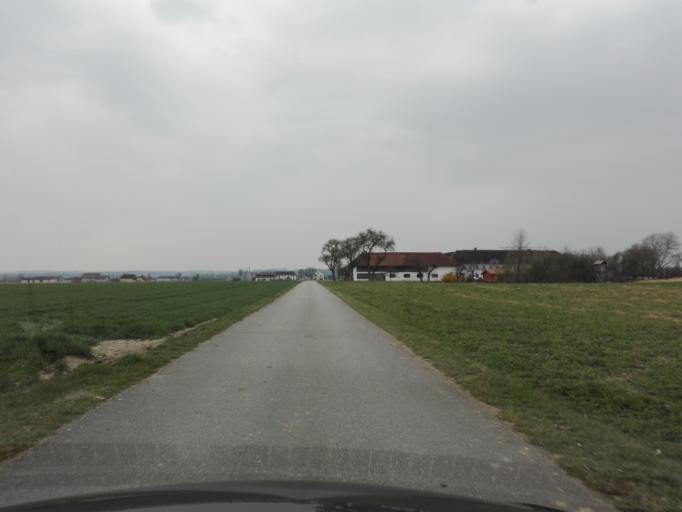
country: AT
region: Upper Austria
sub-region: Politischer Bezirk Perg
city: Perg
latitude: 48.2017
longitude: 14.6718
